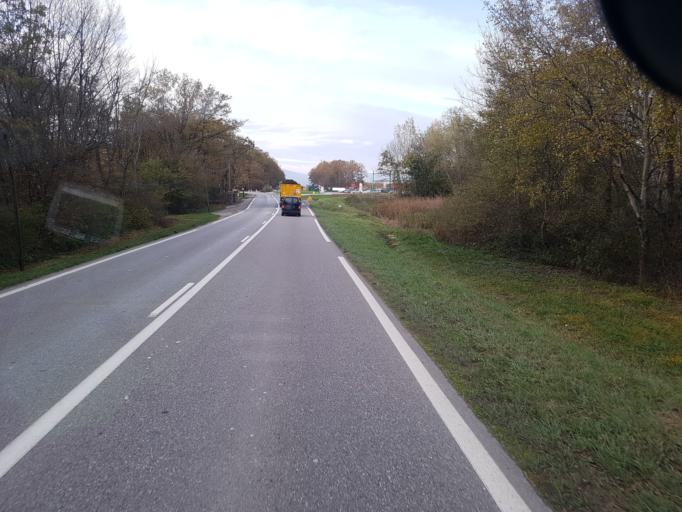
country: FR
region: Rhone-Alpes
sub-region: Departement de l'Ain
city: Bellegarde-sur-Valserine
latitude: 46.0602
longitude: 5.8666
